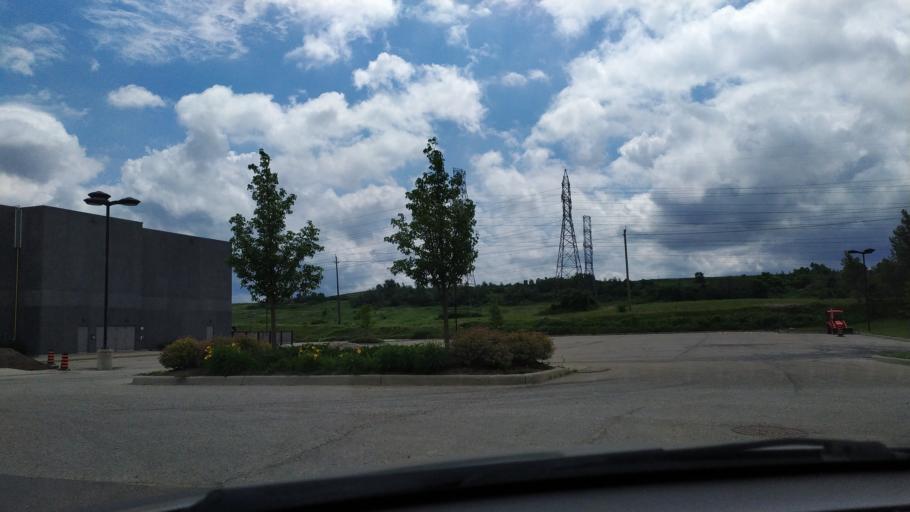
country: CA
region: Ontario
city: Waterloo
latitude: 43.4398
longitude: -80.5670
